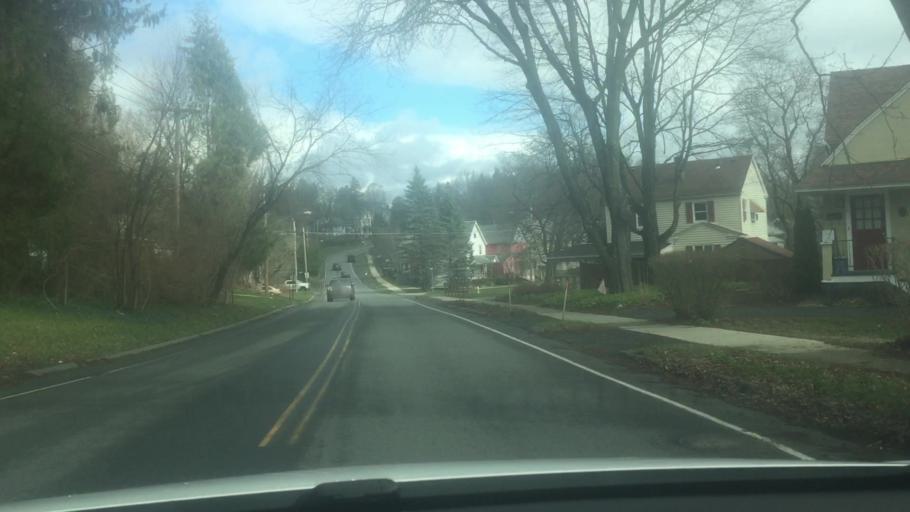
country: US
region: Massachusetts
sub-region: Berkshire County
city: Pittsfield
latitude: 42.4382
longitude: -73.2504
